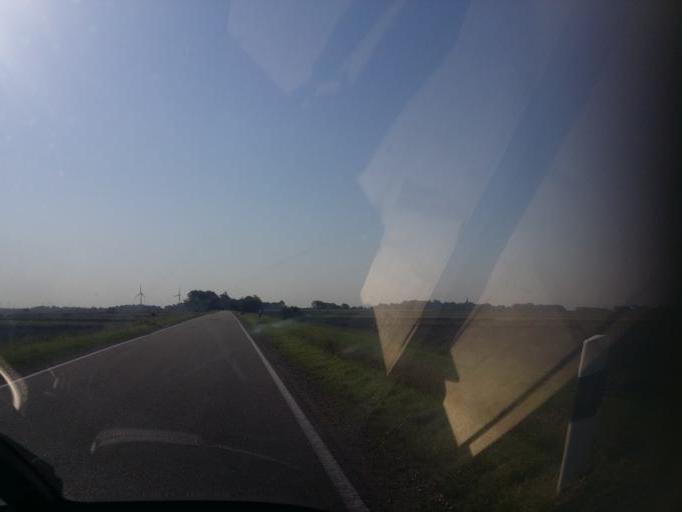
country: DE
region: Schleswig-Holstein
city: Emmelsbull-Horsbull
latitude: 54.7898
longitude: 8.7280
